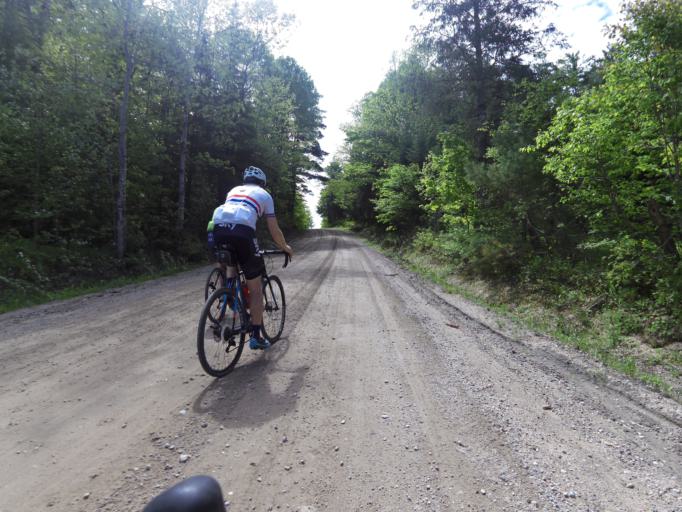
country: CA
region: Quebec
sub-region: Outaouais
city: Wakefield
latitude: 45.7942
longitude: -75.9751
